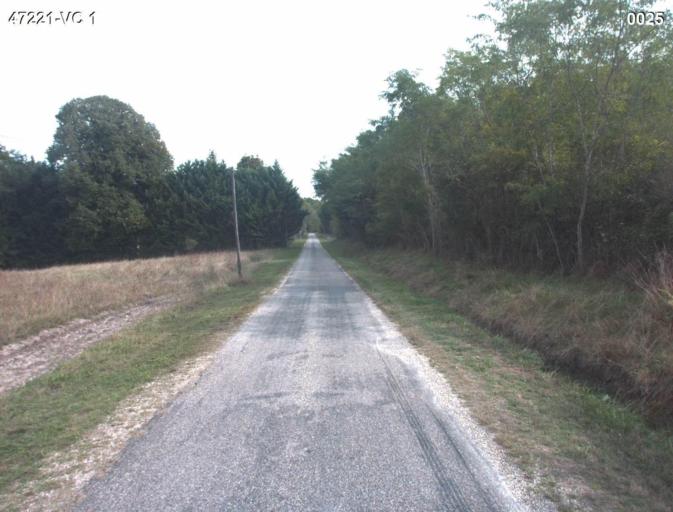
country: FR
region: Aquitaine
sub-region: Departement du Lot-et-Garonne
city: Mezin
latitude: 44.1151
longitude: 0.2184
